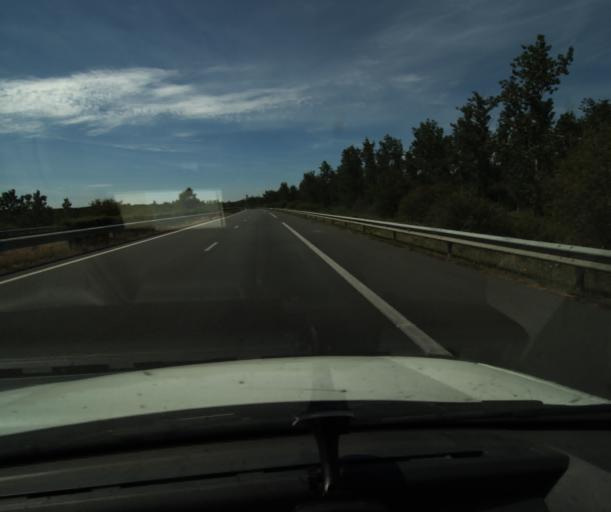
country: FR
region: Midi-Pyrenees
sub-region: Departement du Tarn-et-Garonne
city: Montech
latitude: 44.0012
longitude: 1.2252
